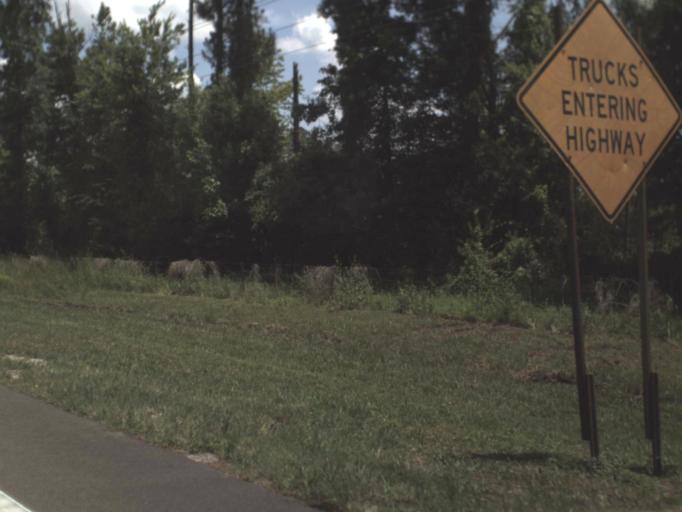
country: US
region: Florida
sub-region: Alachua County
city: Alachua
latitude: 29.8983
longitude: -82.4227
